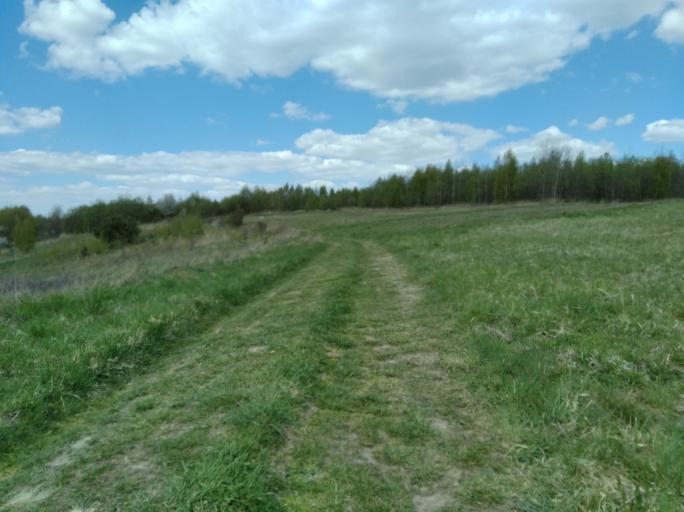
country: PL
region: Subcarpathian Voivodeship
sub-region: Powiat brzozowski
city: Wesola
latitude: 49.7510
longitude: 22.0774
